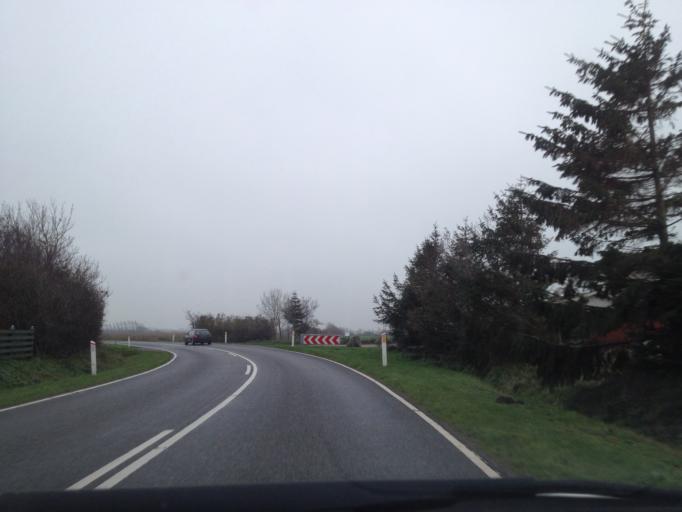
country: DK
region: South Denmark
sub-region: Tonder Kommune
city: Sherrebek
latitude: 55.0729
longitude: 8.7278
